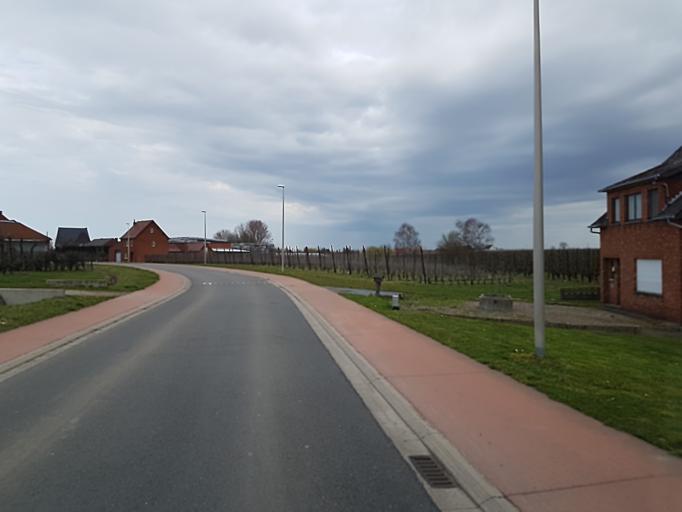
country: BE
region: Flanders
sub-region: Provincie Limburg
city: Nieuwerkerken
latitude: 50.9046
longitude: 5.2379
